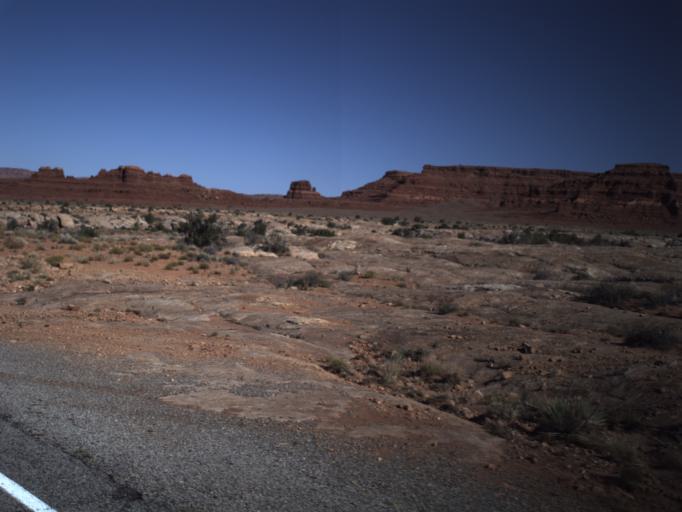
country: US
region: Utah
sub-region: San Juan County
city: Blanding
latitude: 37.8185
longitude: -110.3471
